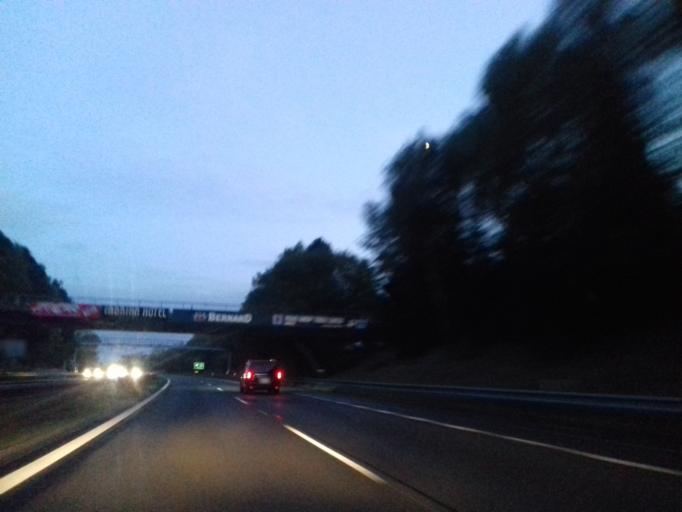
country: CZ
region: Vysocina
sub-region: Okres Pelhrimov
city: Humpolec
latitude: 49.5340
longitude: 15.3347
